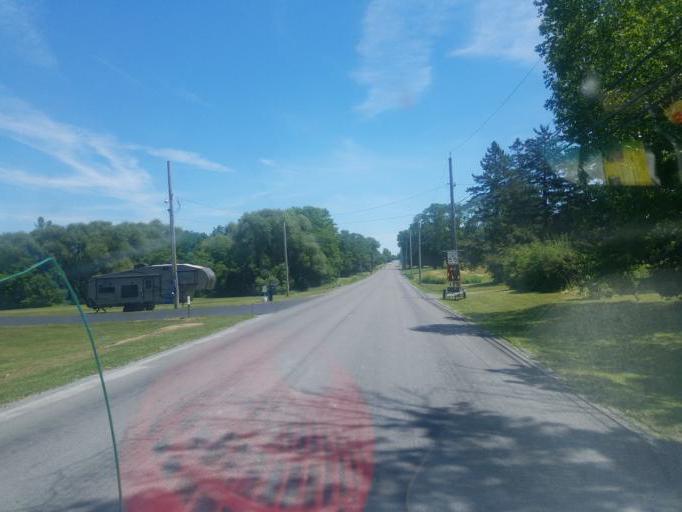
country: US
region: New York
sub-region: Yates County
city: Penn Yan
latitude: 42.6521
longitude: -77.0333
